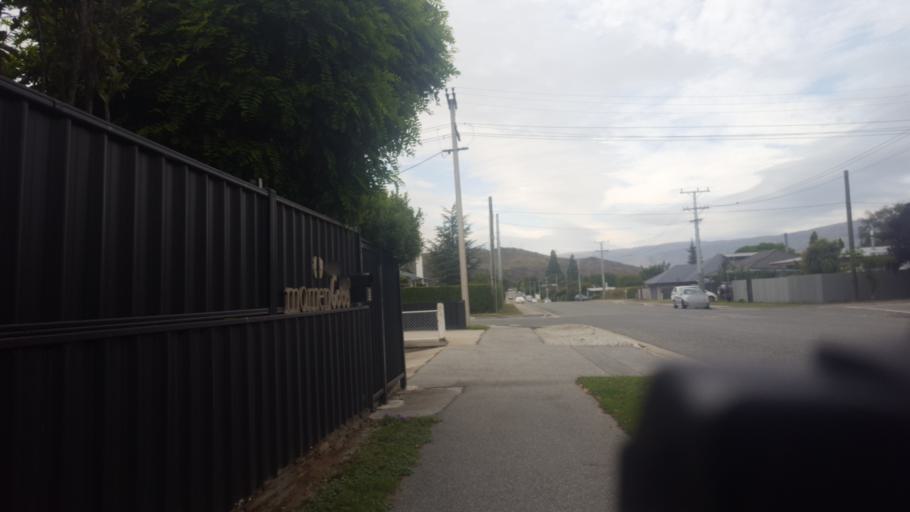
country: NZ
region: Otago
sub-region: Queenstown-Lakes District
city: Wanaka
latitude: -45.0426
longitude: 169.2119
